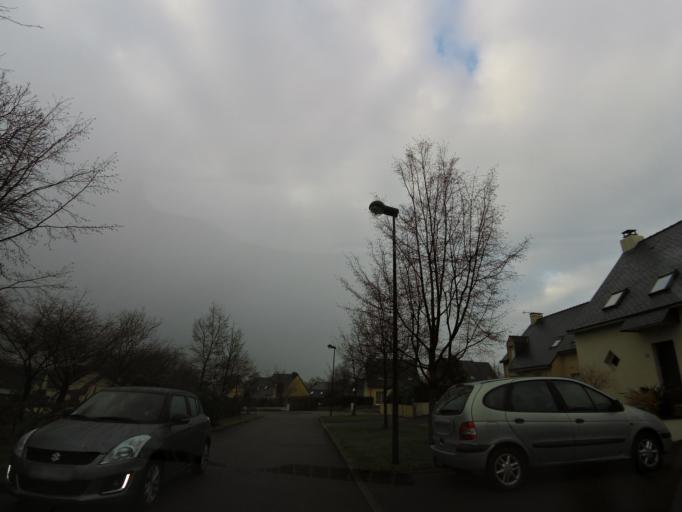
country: FR
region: Brittany
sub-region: Departement d'Ille-et-Vilaine
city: Laille
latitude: 47.9763
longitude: -1.7124
